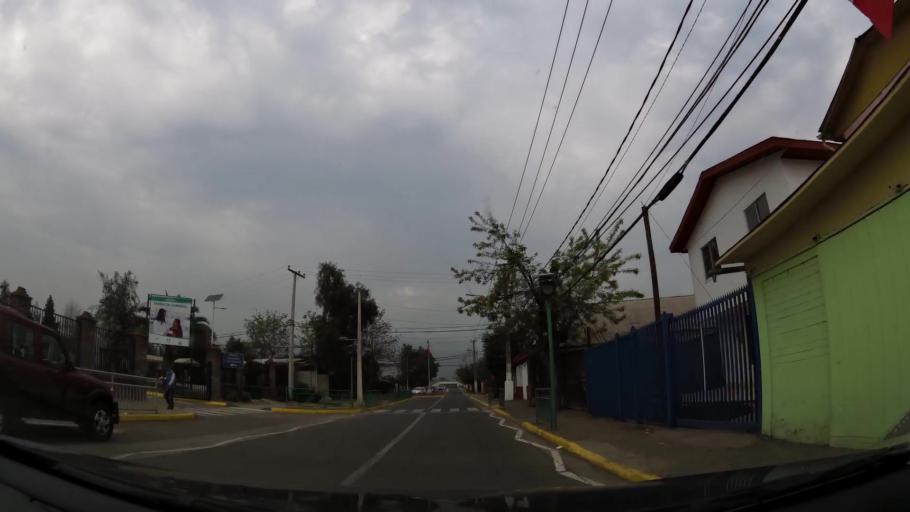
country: CL
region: Santiago Metropolitan
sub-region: Provincia de Chacabuco
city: Chicureo Abajo
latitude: -33.2067
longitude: -70.6706
